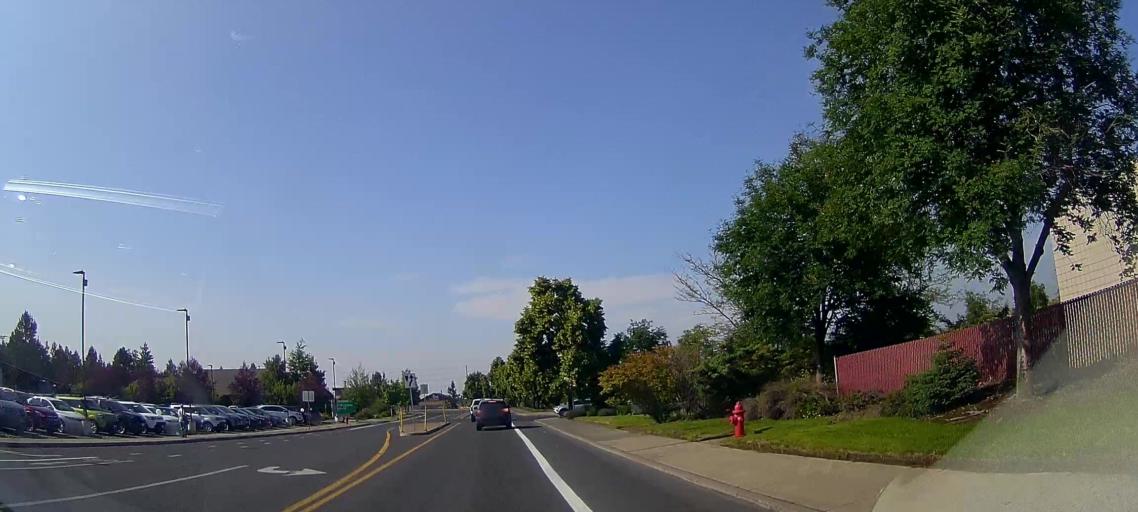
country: US
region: Oregon
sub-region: Deschutes County
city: Bend
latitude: 44.0558
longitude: -121.2686
